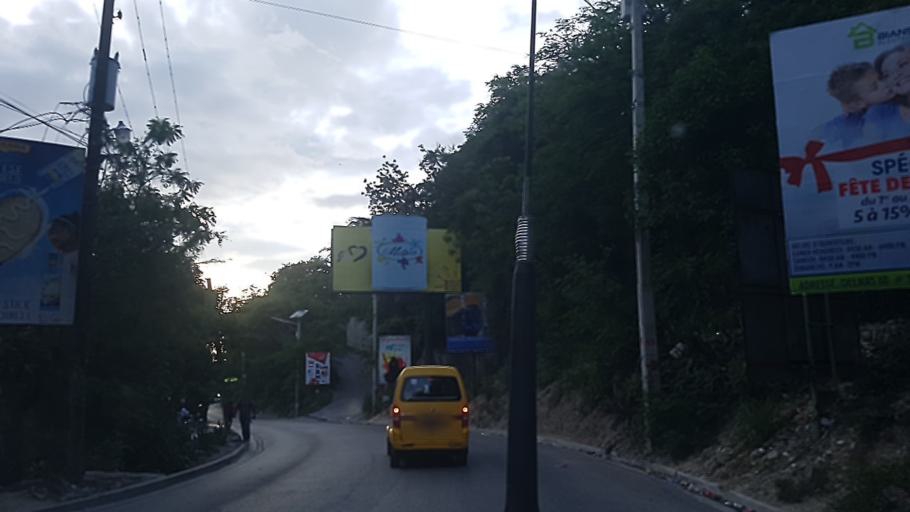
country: HT
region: Ouest
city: Petionville
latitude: 18.5256
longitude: -72.2974
